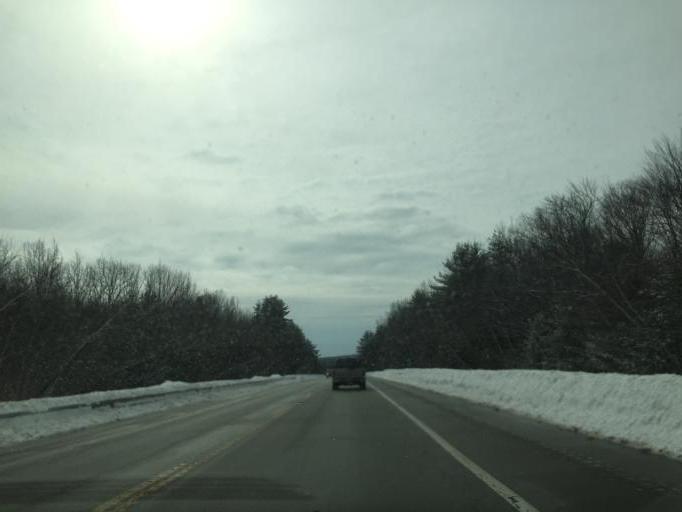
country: US
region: New Hampshire
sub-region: Strafford County
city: Rochester
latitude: 43.3581
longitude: -70.9866
